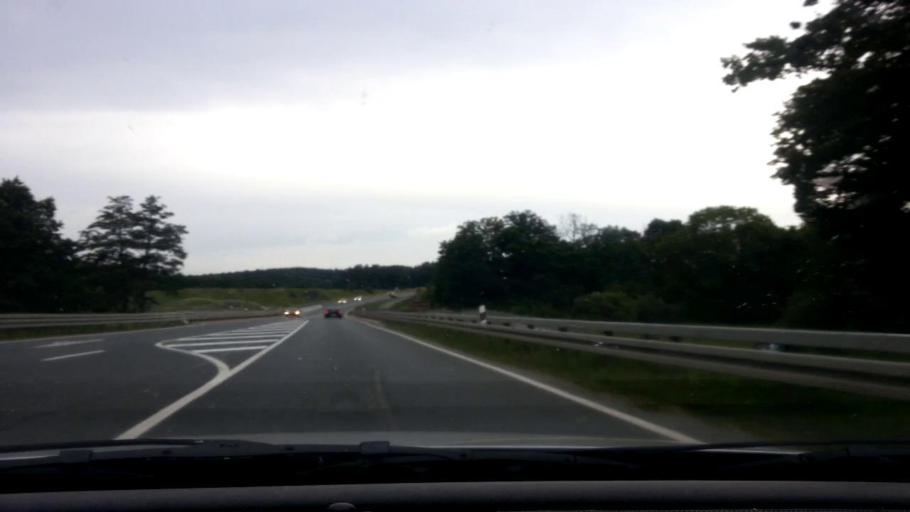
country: DE
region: Bavaria
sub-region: Upper Franconia
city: Neunkirchen am Main
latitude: 49.9205
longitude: 11.6394
